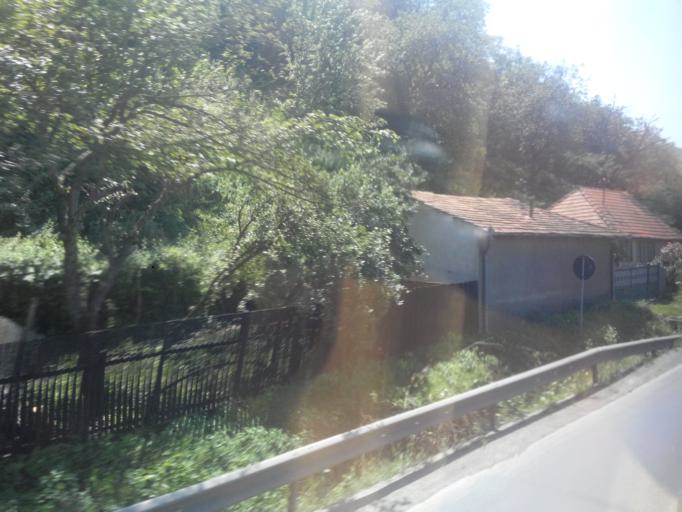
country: RO
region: Hunedoara
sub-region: Comuna Ilia
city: Ilia
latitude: 45.9228
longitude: 22.6760
